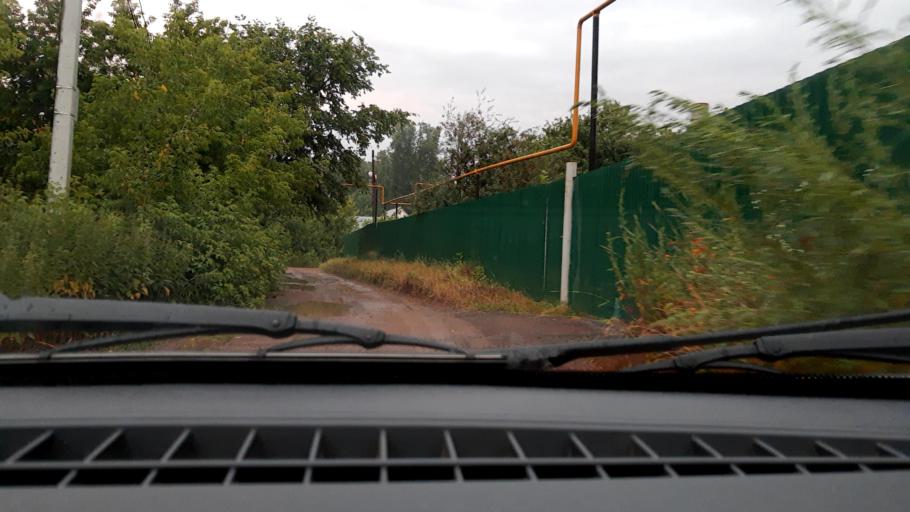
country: RU
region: Bashkortostan
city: Ufa
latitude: 54.7570
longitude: 55.9239
